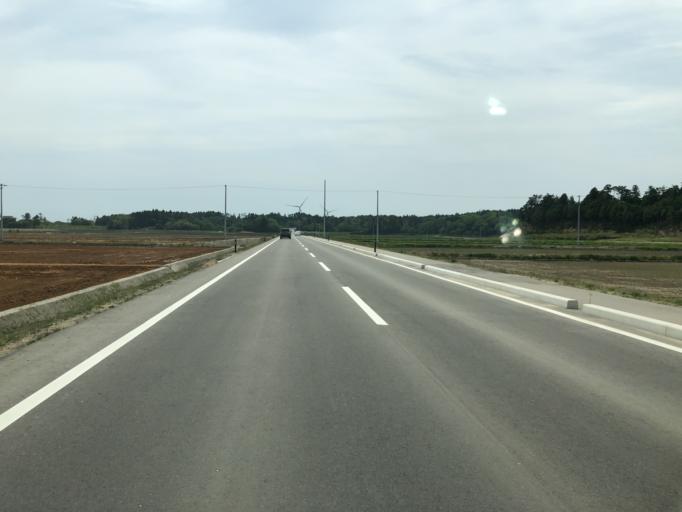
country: JP
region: Fukushima
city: Namie
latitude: 37.7180
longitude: 141.0040
